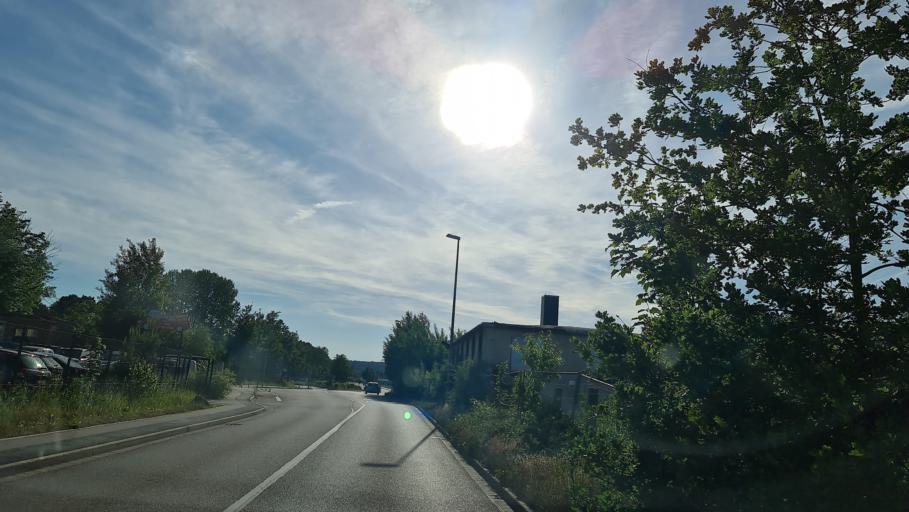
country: DE
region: Saxony
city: Wittgensdorf
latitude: 50.8324
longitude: 12.8619
